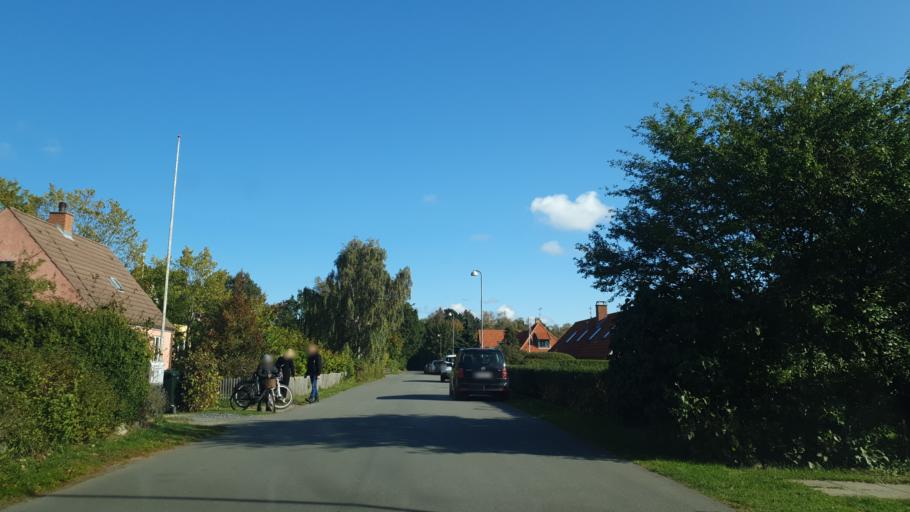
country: DK
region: Zealand
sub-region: Odsherred Kommune
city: Nykobing Sjaelland
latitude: 55.9456
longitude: 11.7592
